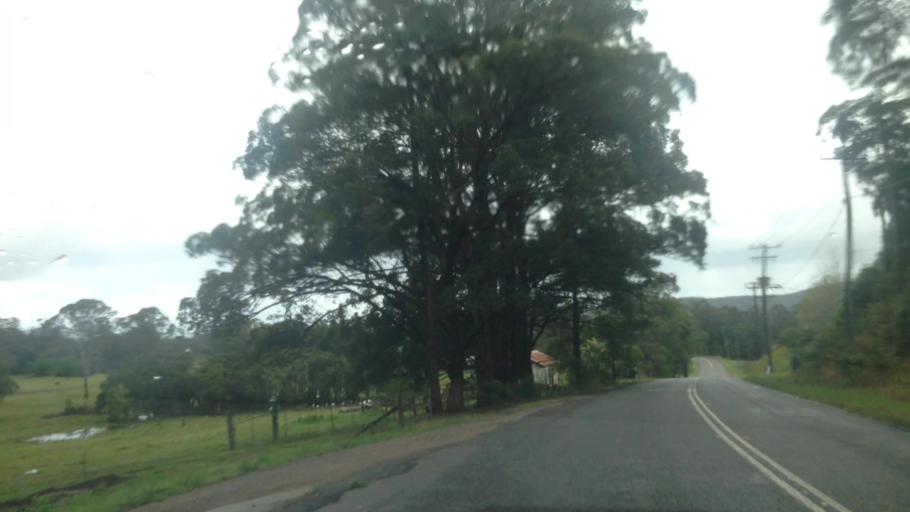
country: AU
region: New South Wales
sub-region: Wyong Shire
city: Little Jilliby
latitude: -33.2484
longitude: 151.3836
